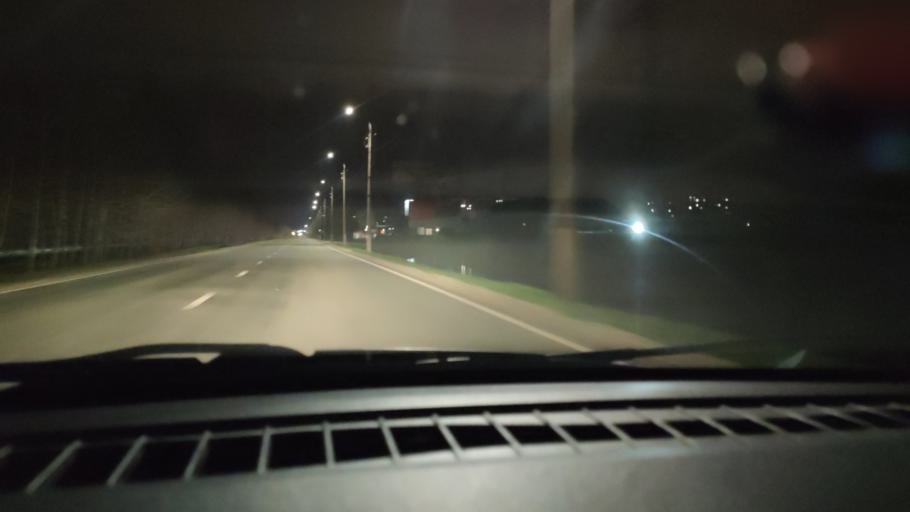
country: RU
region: Bashkortostan
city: Sterlitamak
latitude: 53.6452
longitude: 55.8882
